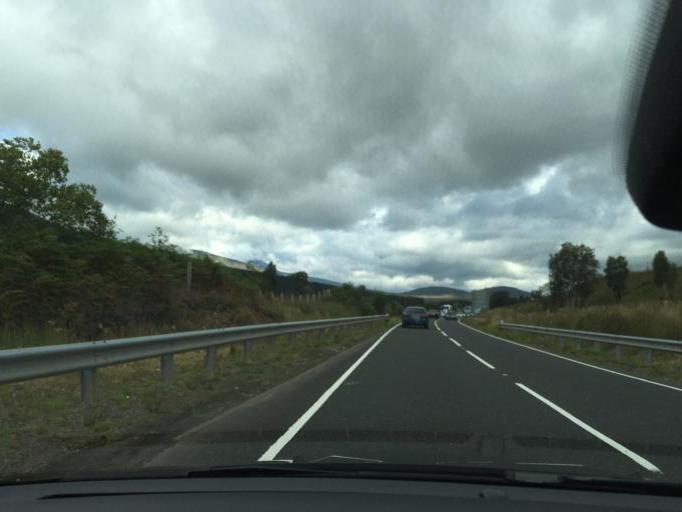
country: GB
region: Scotland
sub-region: Highland
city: Spean Bridge
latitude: 56.5065
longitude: -4.7681
